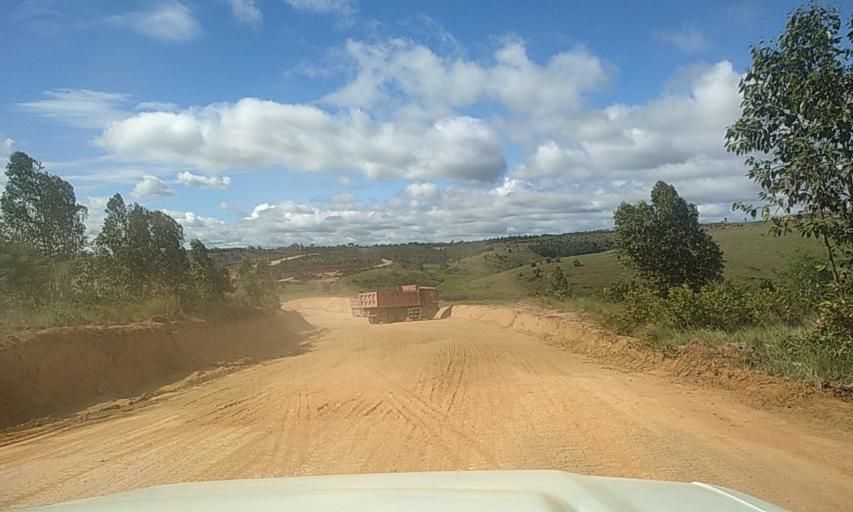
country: MG
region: Alaotra Mangoro
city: Ambatondrazaka
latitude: -18.0226
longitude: 48.2573
